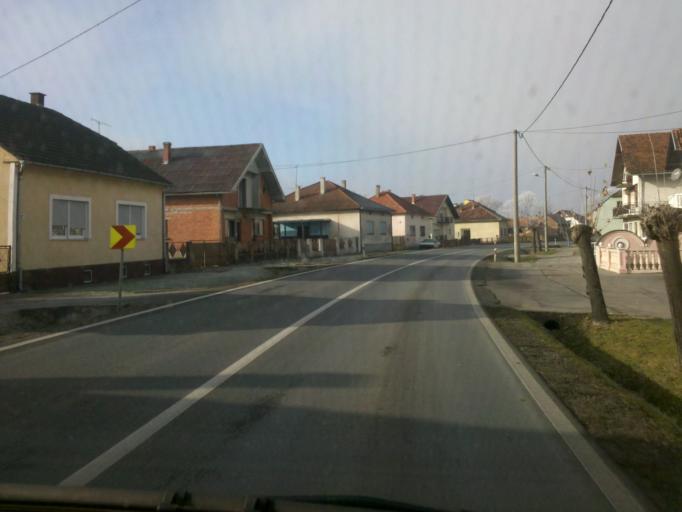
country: HR
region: Virovitick-Podravska
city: Pitomaca
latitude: 45.9573
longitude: 17.2269
